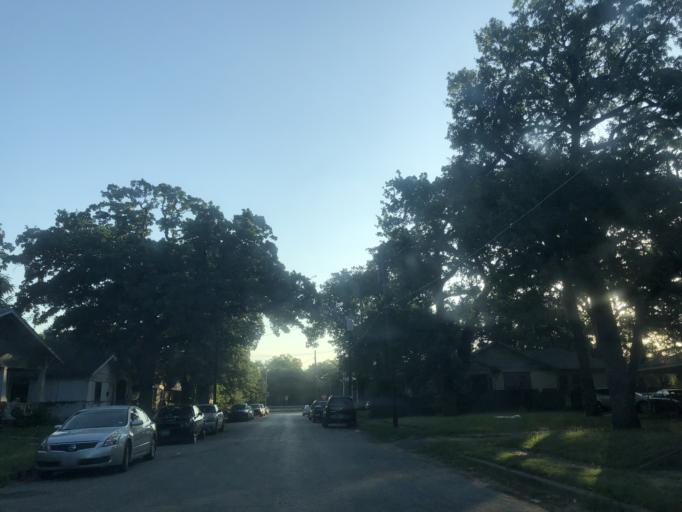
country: US
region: Texas
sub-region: Dallas County
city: Dallas
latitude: 32.7542
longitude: -96.7674
